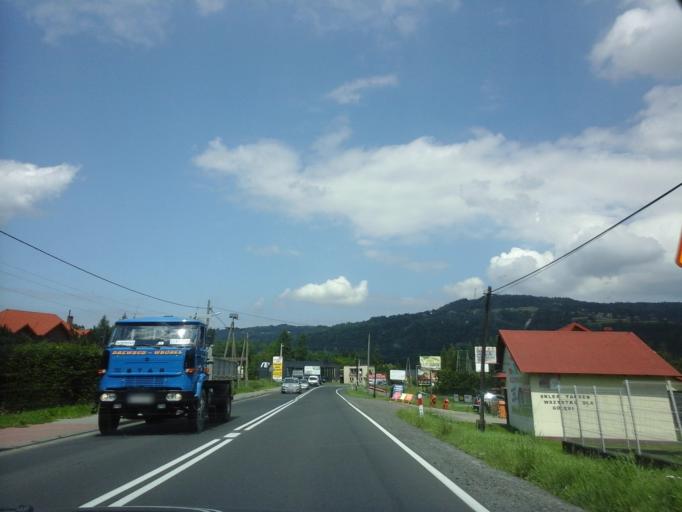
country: PL
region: Lesser Poland Voivodeship
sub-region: Powiat suski
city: Makow Podhalanski
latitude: 49.7177
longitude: 19.6878
